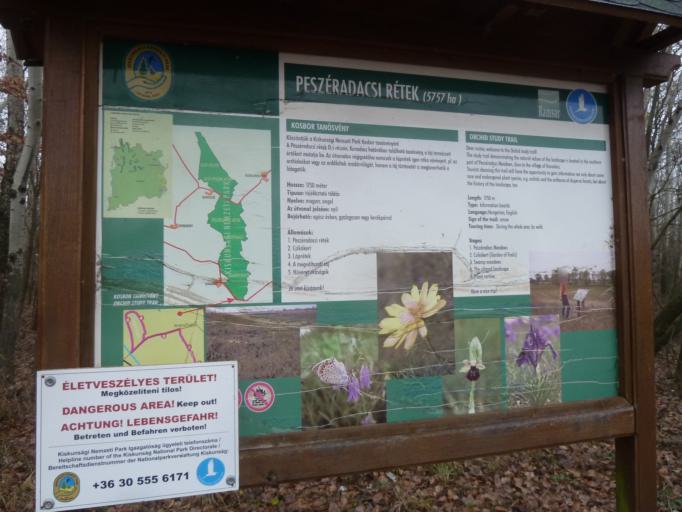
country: HU
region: Bacs-Kiskun
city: Szabadszallas
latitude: 46.9349
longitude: 19.3263
